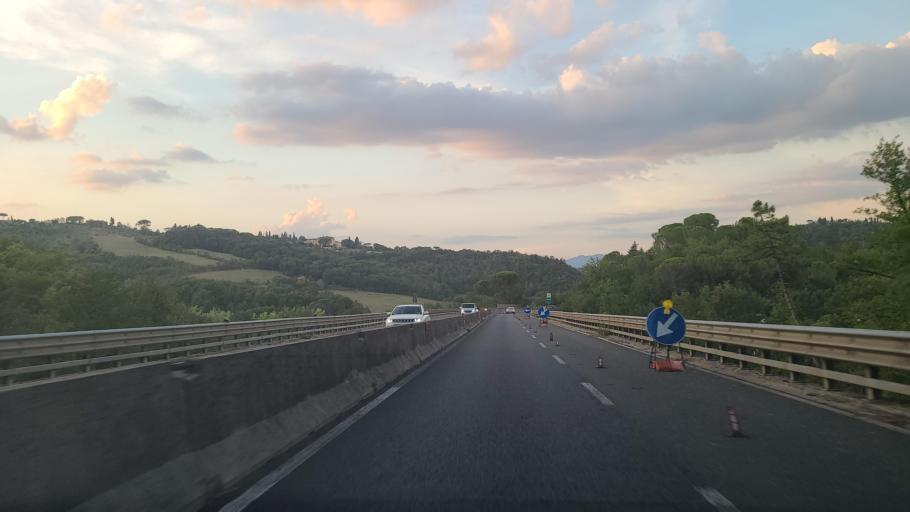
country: IT
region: Tuscany
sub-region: Province of Florence
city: San Casciano in Val di Pesa
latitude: 43.6746
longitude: 11.2102
